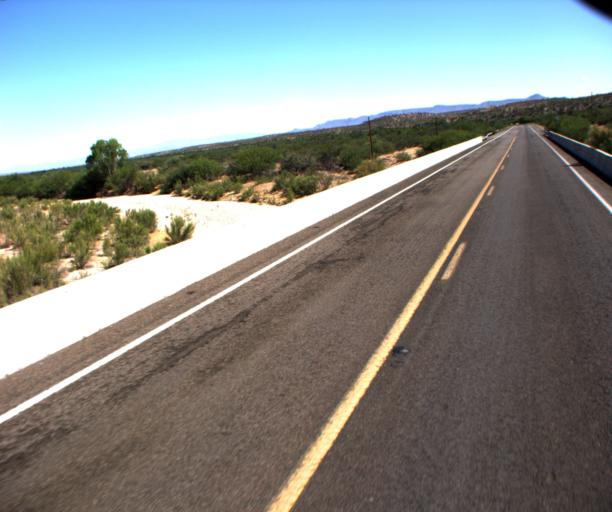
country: US
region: Arizona
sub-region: Pinal County
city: Mammoth
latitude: 32.7422
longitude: -110.6481
